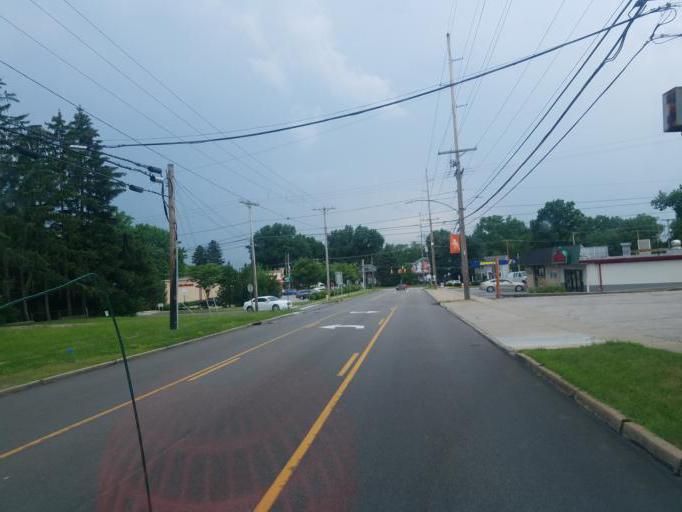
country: US
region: Ohio
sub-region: Medina County
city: Wadsworth
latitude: 41.0364
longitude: -81.7271
